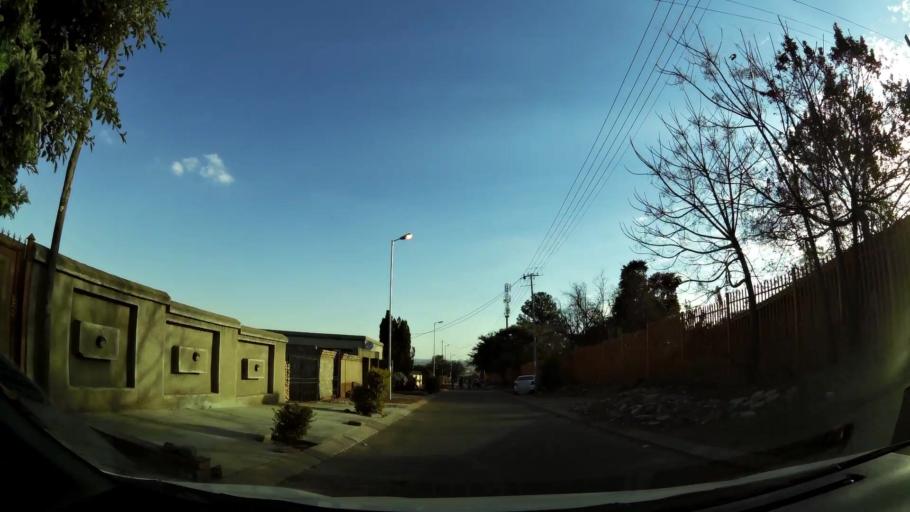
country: ZA
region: Gauteng
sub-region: City of Tshwane Metropolitan Municipality
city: Cullinan
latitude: -25.7053
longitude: 28.3835
